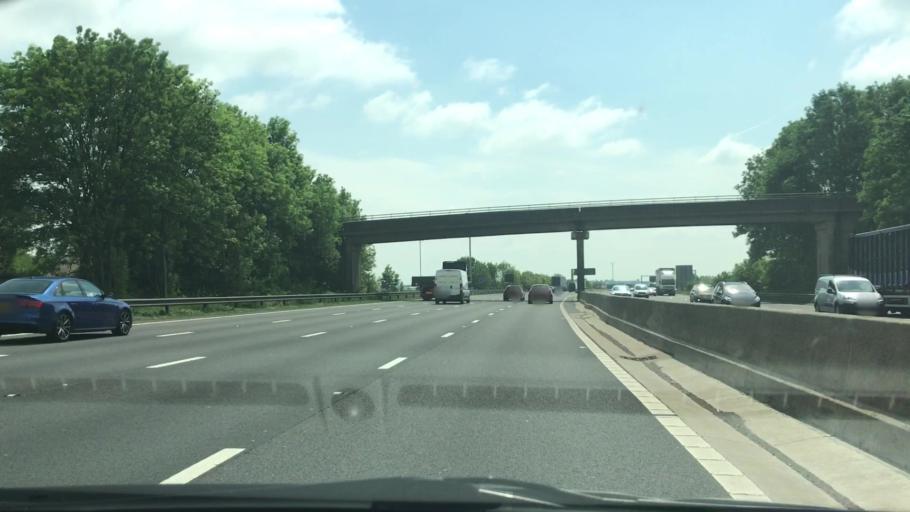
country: GB
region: England
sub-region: Derbyshire
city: Blackwell
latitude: 53.1306
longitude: -1.3290
